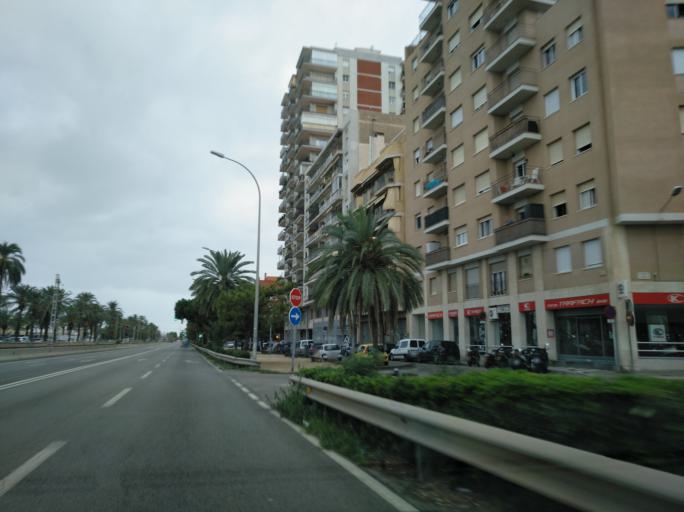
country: ES
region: Catalonia
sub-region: Provincia de Barcelona
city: Mataro
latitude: 41.5399
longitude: 2.4545
